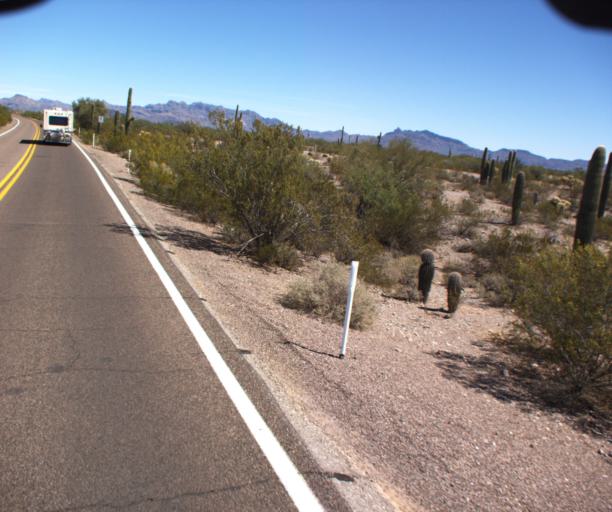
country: MX
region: Sonora
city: Sonoyta
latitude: 31.8842
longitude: -112.8144
